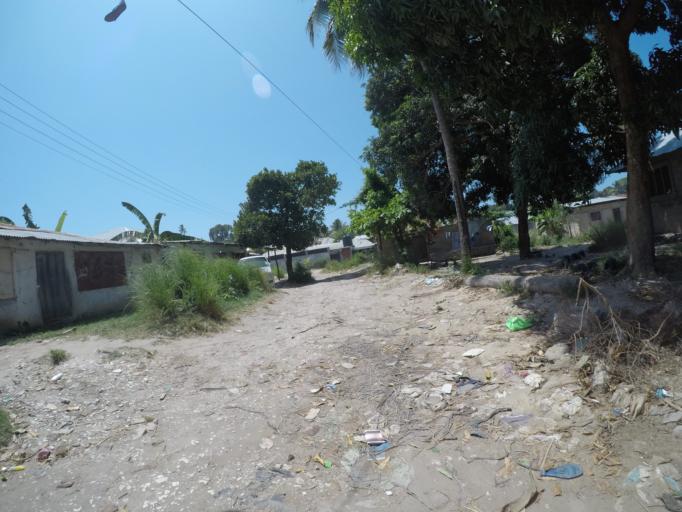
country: TZ
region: Zanzibar Urban/West
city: Zanzibar
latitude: -6.1785
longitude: 39.2059
